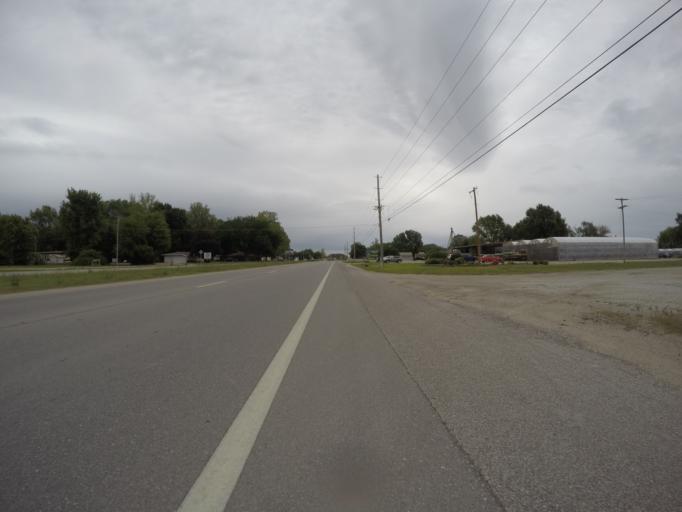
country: US
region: Kansas
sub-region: Riley County
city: Manhattan
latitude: 39.1958
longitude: -96.5190
